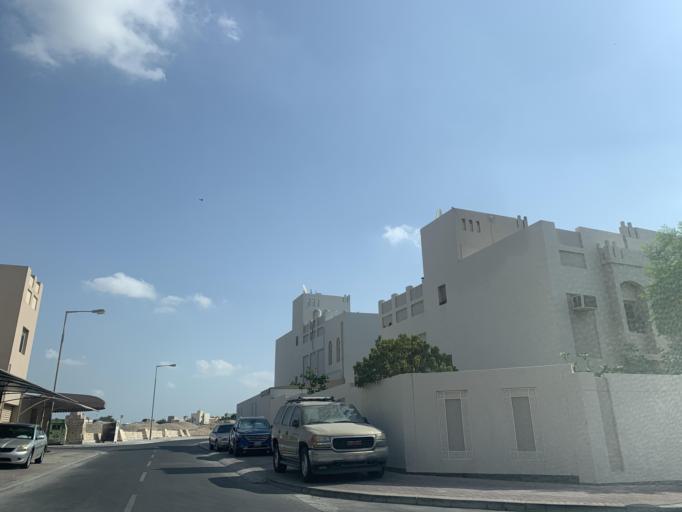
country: BH
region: Central Governorate
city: Madinat Hamad
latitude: 26.1406
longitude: 50.5003
